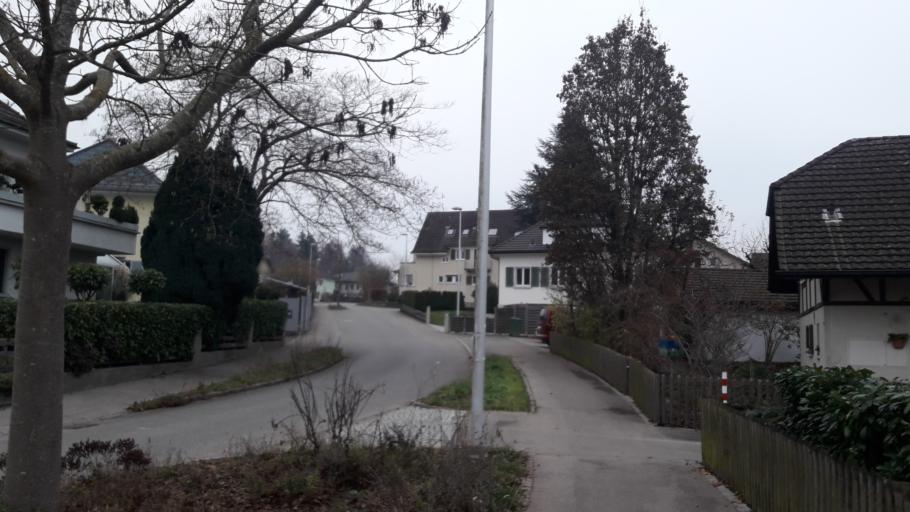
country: CH
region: Solothurn
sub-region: Bezirk Wasseramt
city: Zuchwil
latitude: 47.1977
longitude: 7.5512
